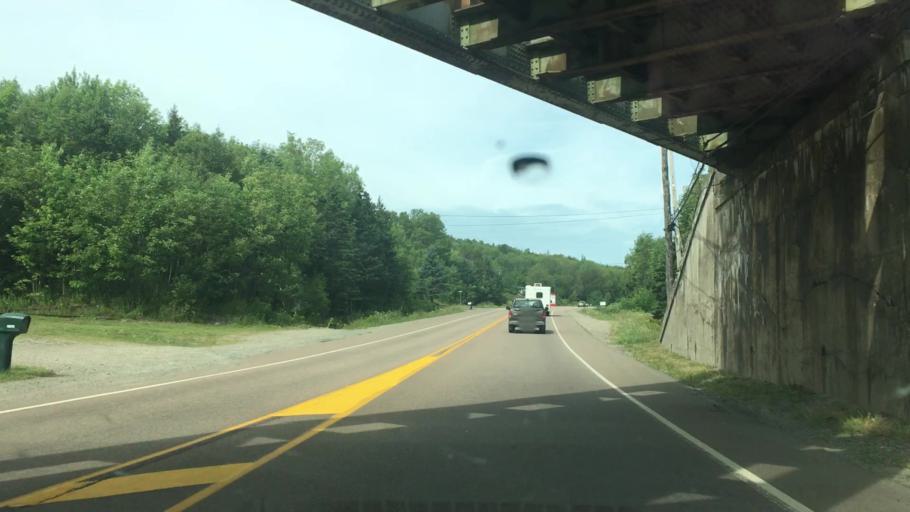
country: CA
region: Nova Scotia
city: Port Hawkesbury
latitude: 45.6543
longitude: -61.4468
